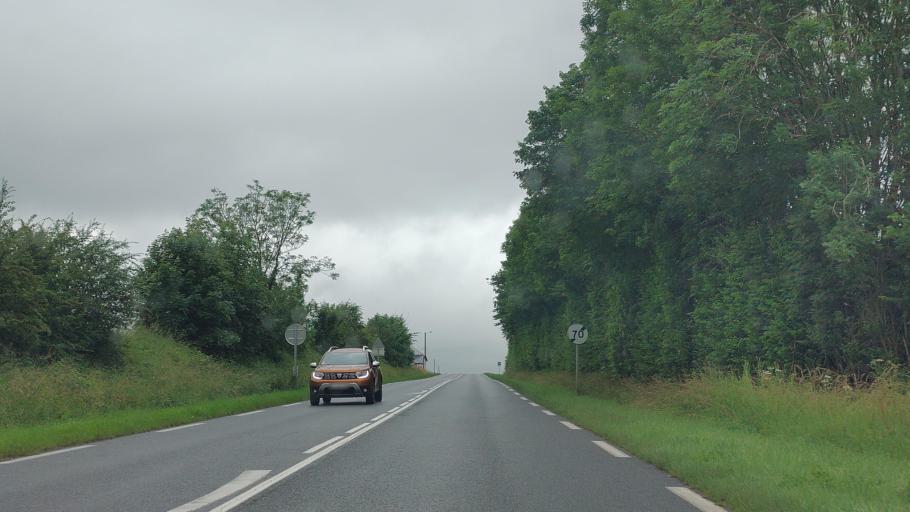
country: FR
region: Picardie
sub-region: Departement de la Somme
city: Chepy
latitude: 50.0863
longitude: 1.6658
